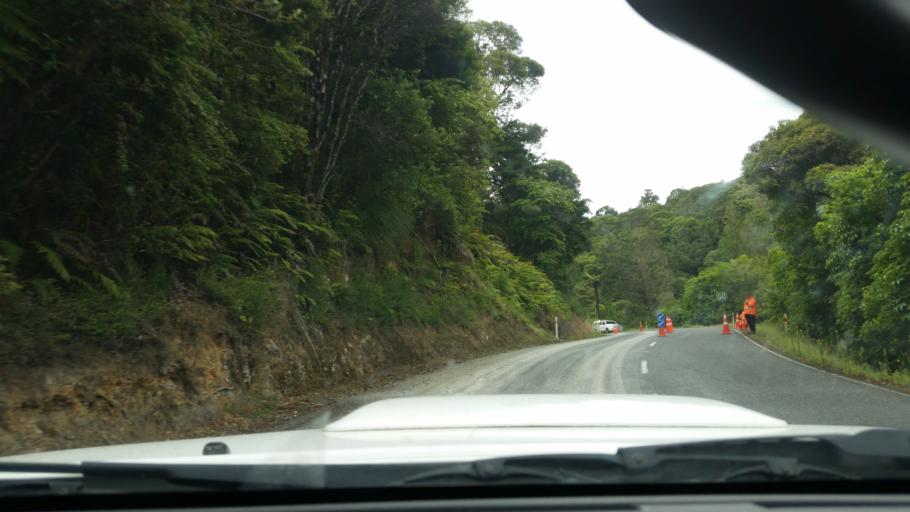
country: NZ
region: Northland
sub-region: Kaipara District
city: Dargaville
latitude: -35.7175
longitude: 173.8581
